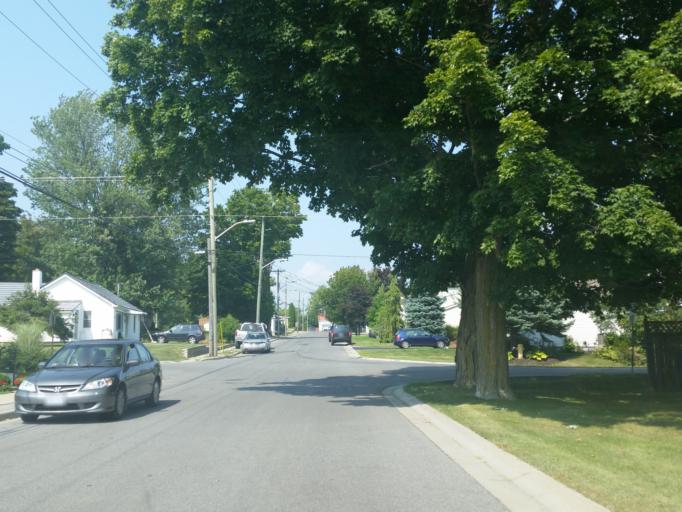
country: CA
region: Ontario
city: Picton
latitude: 44.0093
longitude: -77.1306
